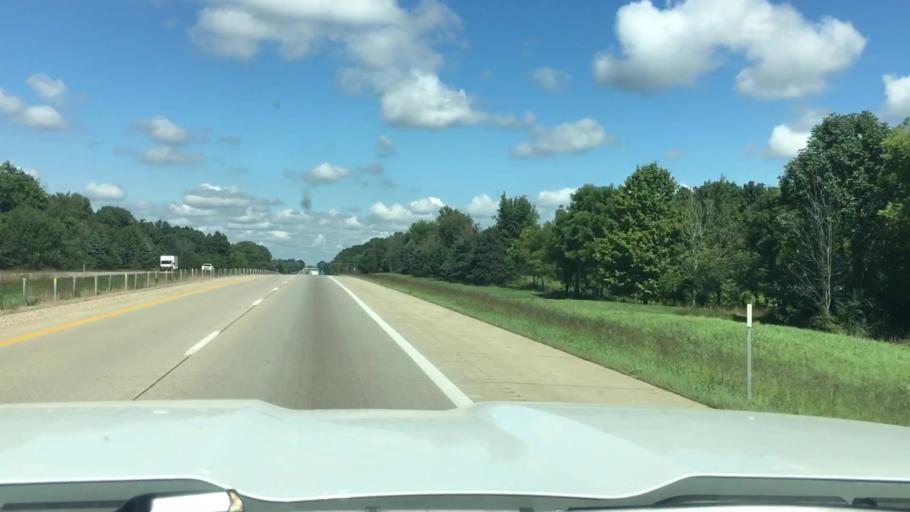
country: US
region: Michigan
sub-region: Allegan County
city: Otsego
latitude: 42.5043
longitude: -85.6535
